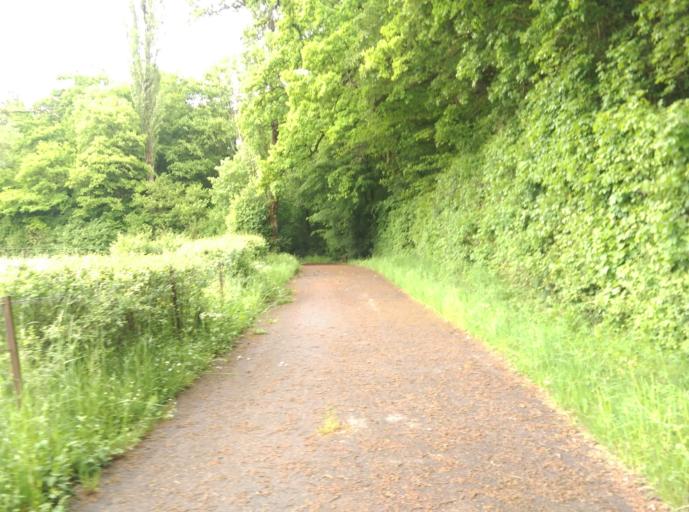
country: LU
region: Luxembourg
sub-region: Canton de Luxembourg
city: Niederanven
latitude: 49.6639
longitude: 6.2583
